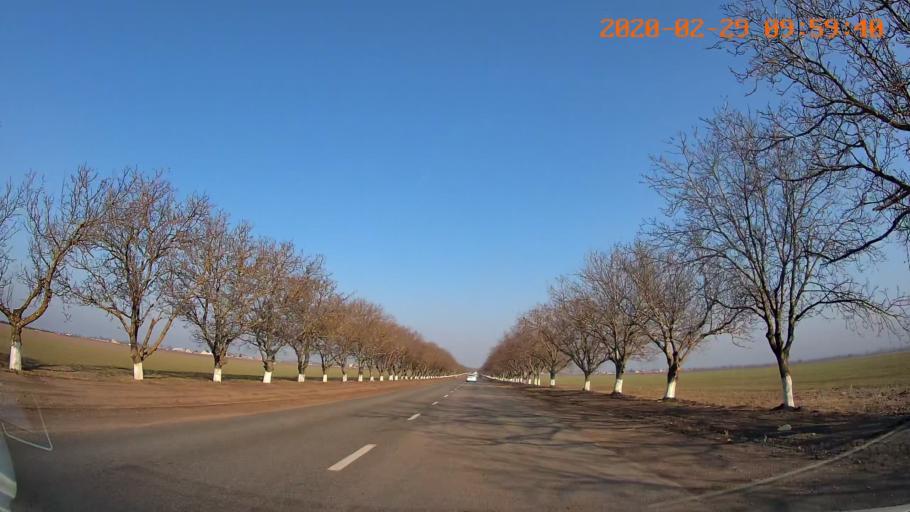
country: MD
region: Telenesti
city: Slobozia
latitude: 46.7594
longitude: 29.6879
